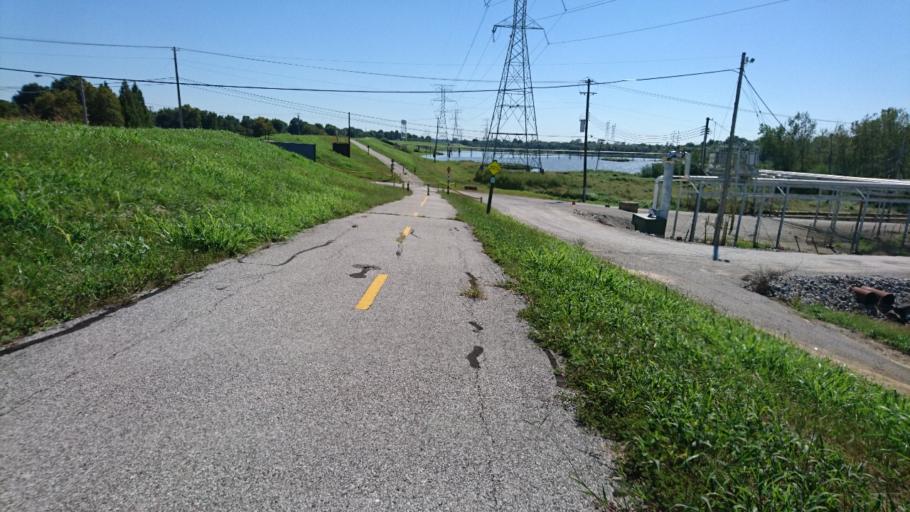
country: US
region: Illinois
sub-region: Madison County
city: Hartford
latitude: 38.8415
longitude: -90.0982
